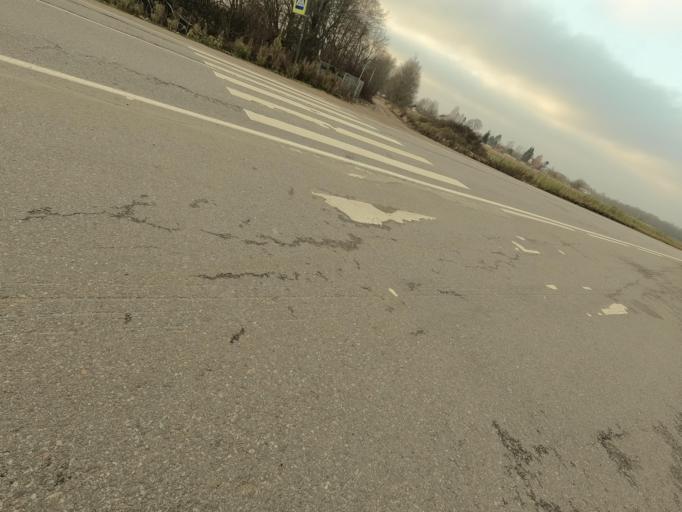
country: RU
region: Leningrad
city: Mga
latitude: 59.7541
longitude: 31.0351
